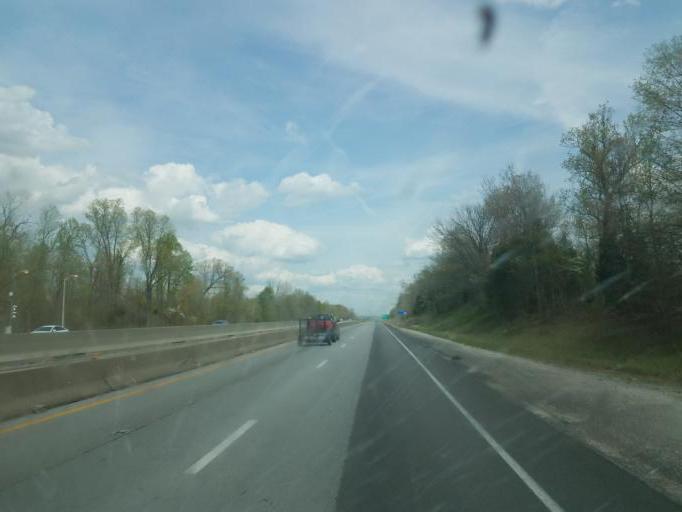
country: US
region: Kentucky
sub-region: Hardin County
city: Elizabethtown
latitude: 37.6557
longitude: -85.8558
